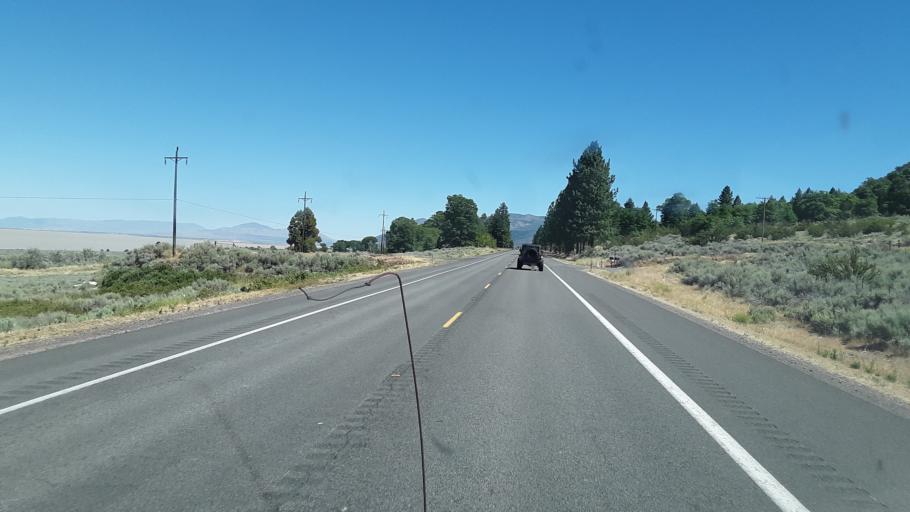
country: US
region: California
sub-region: Lassen County
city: Janesville
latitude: 40.2247
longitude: -120.4365
